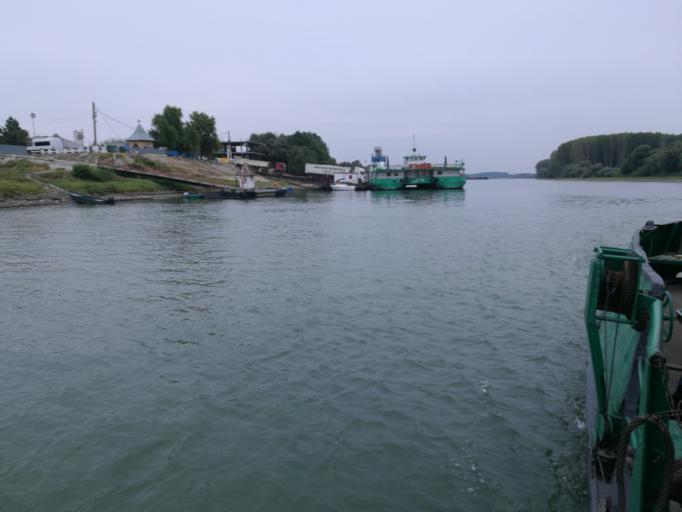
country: RO
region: Braila
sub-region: Municipiul Braila
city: Braila
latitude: 45.2862
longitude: 27.9964
